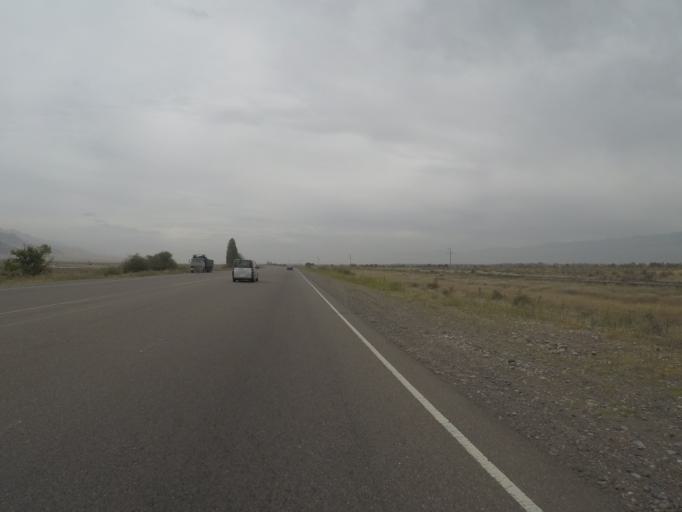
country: KG
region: Chuy
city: Tokmok
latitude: 42.8306
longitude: 75.4594
